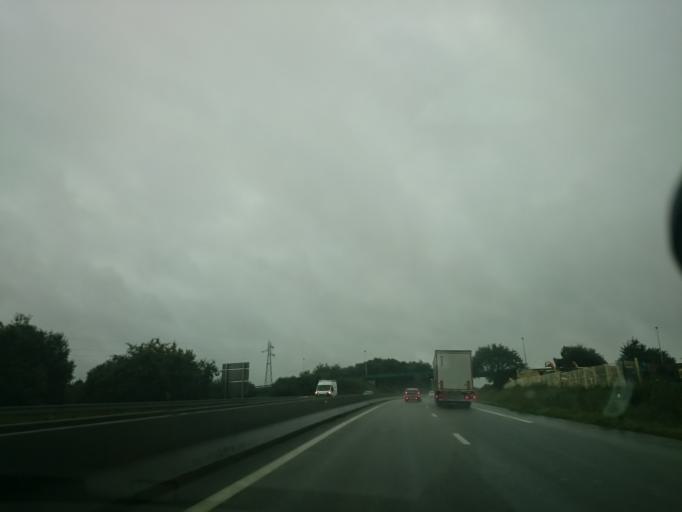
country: FR
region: Brittany
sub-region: Departement du Morbihan
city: Vannes
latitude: 47.6608
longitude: -2.7084
